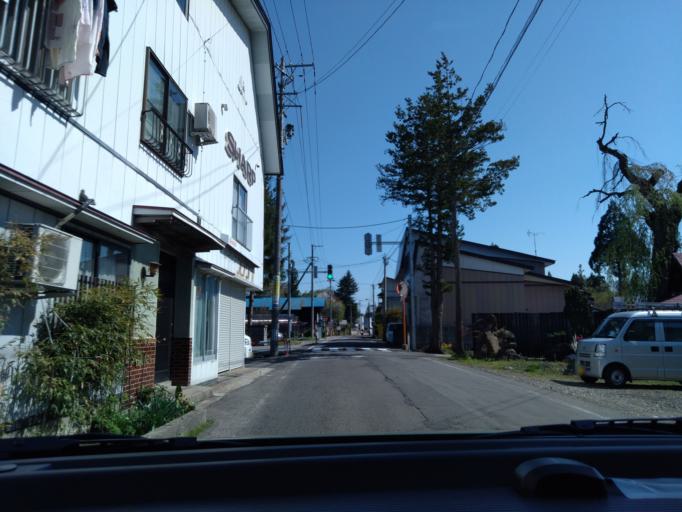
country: JP
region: Akita
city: Kakunodatemachi
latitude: 39.5582
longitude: 140.5853
